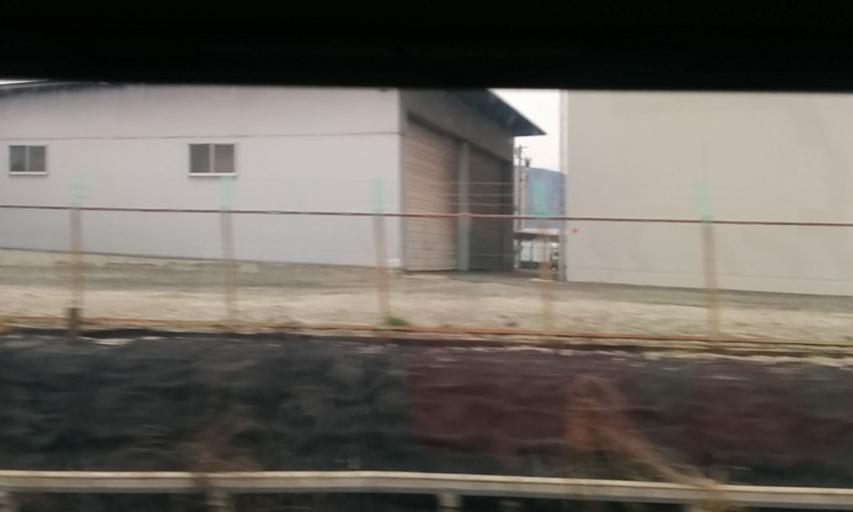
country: JP
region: Nagano
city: Shiojiri
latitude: 36.1342
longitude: 137.9489
